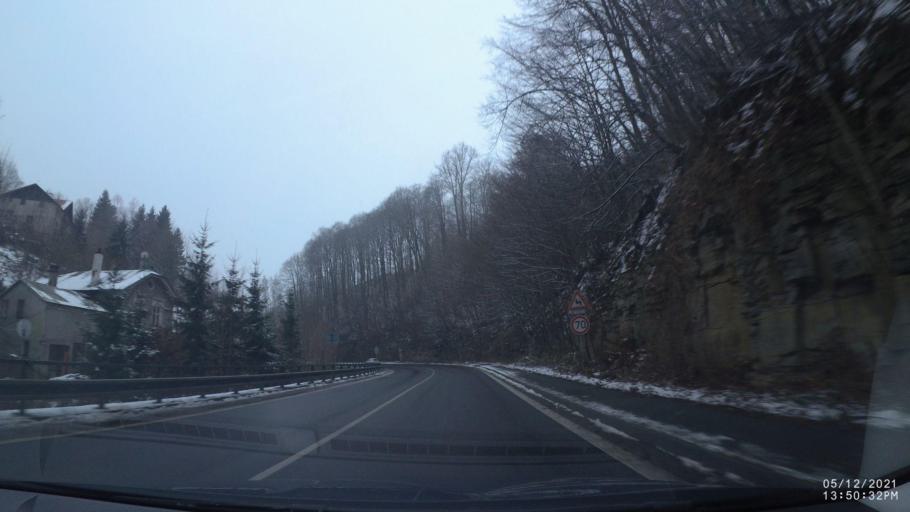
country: CZ
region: Kralovehradecky
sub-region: Okres Nachod
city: Police nad Metuji
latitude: 50.5353
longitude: 16.2281
